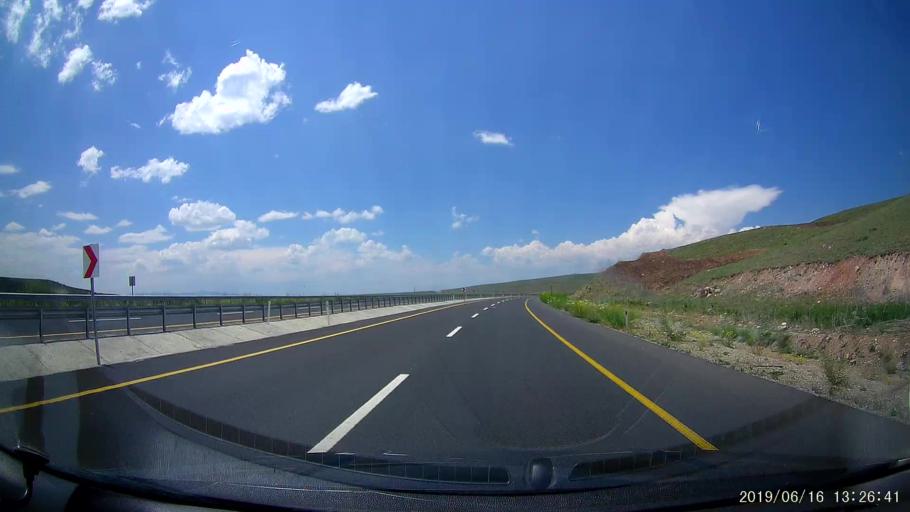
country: TR
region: Agri
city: Taslicay
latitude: 39.6605
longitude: 43.3228
